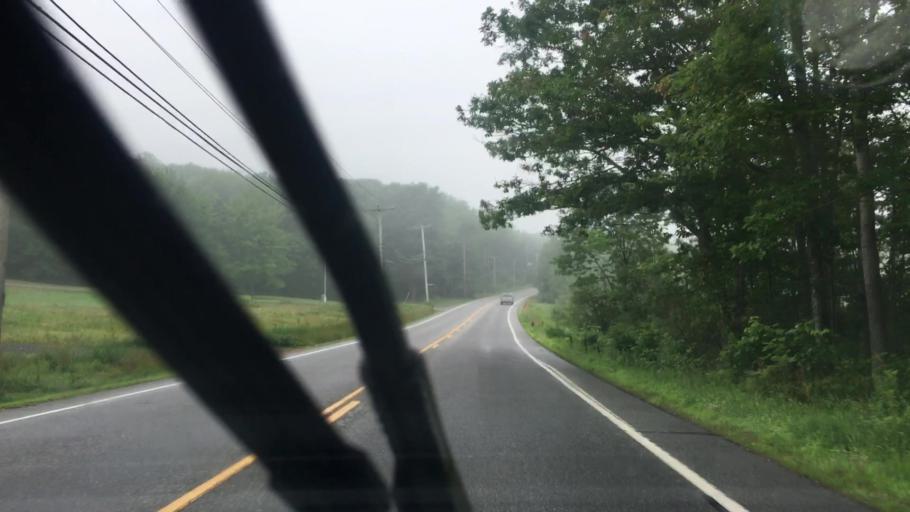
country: US
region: Maine
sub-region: Lincoln County
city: Boothbay
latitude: 43.8886
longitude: -69.6294
